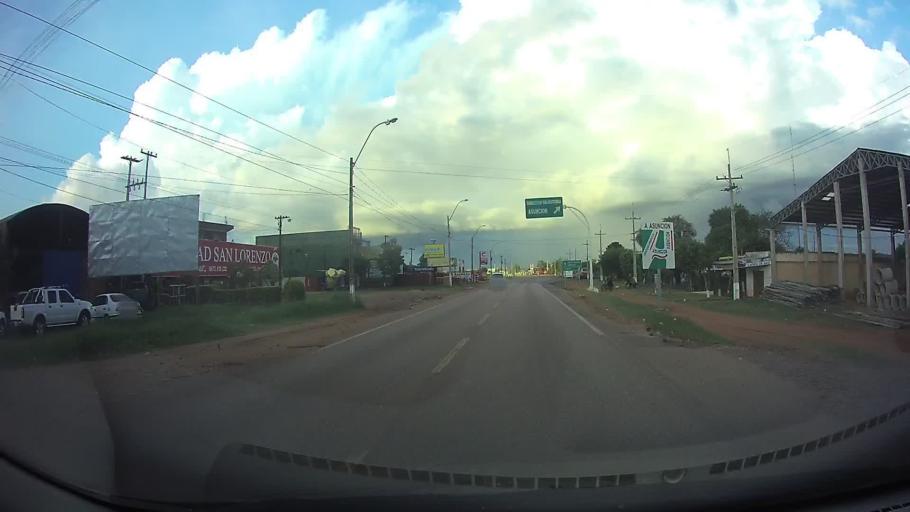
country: PY
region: Paraguari
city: Carapegua
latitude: -25.7653
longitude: -57.2359
